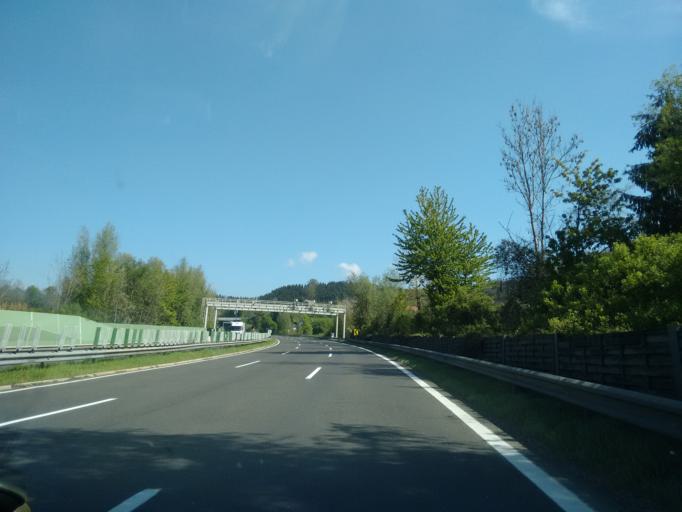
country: AT
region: Styria
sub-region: Politischer Bezirk Leoben
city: Leoben
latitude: 47.3626
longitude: 15.1085
